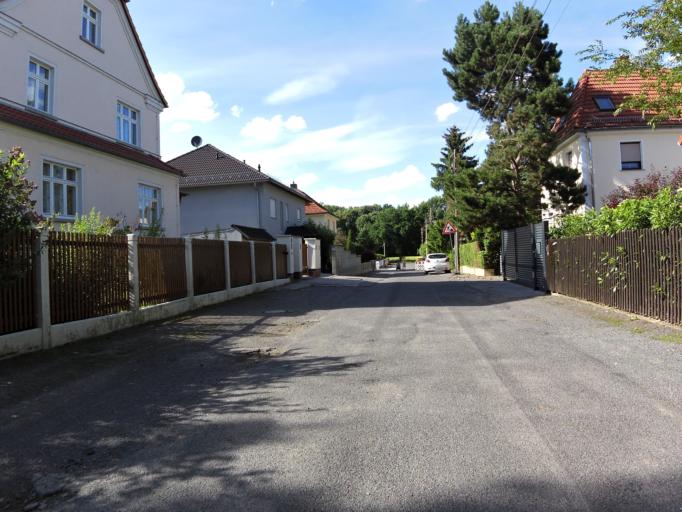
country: DE
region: Saxony
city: Taucha
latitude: 51.3257
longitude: 12.4579
